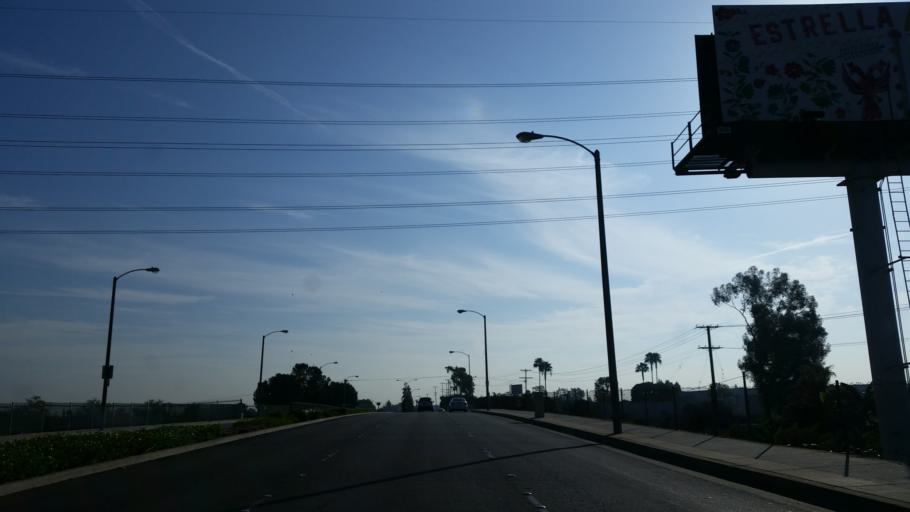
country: US
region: California
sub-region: Los Angeles County
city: Bellflower
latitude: 33.8878
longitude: -118.1102
